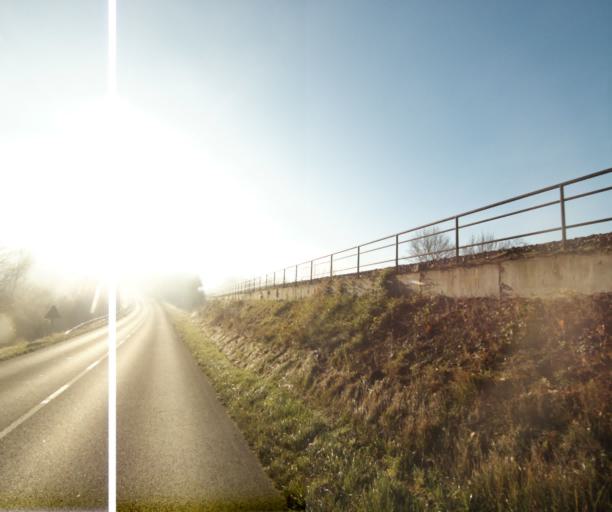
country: FR
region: Poitou-Charentes
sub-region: Departement de la Charente-Maritime
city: Bussac-sur-Charente
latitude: 45.7771
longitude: -0.6255
